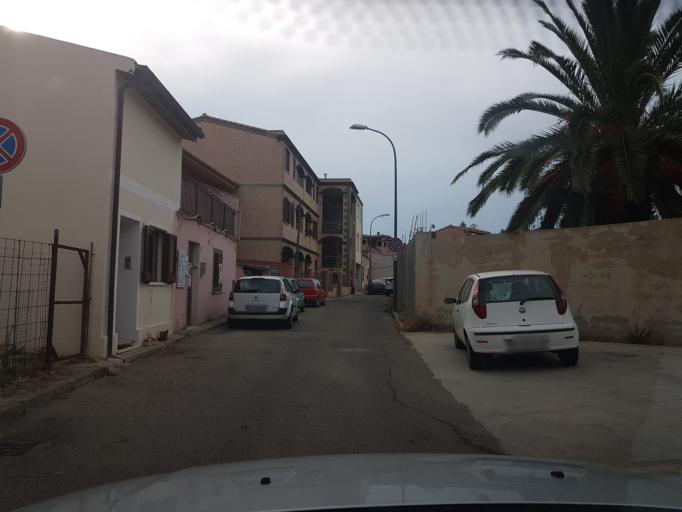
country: IT
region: Sardinia
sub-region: Provincia di Oristano
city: Donigala Fenugheddu
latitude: 39.9264
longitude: 8.5752
